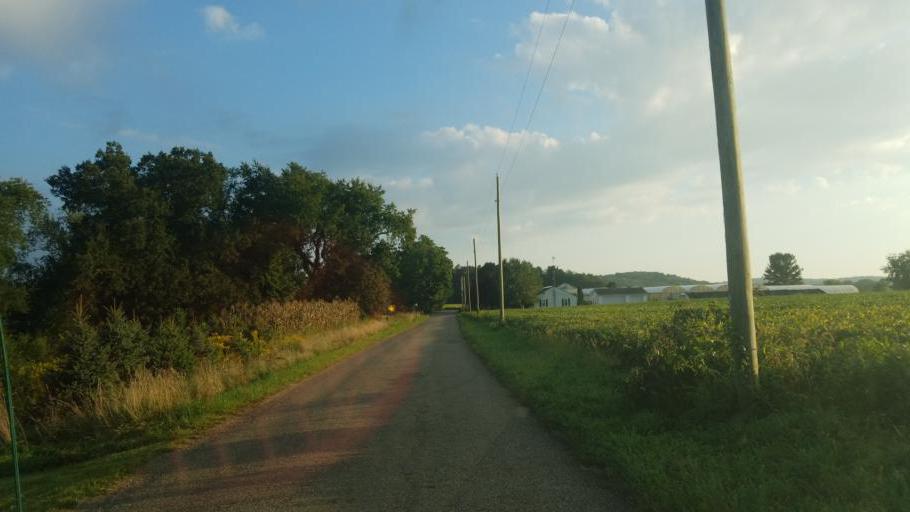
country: US
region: Ohio
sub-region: Ashland County
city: Loudonville
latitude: 40.6555
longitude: -82.1981
